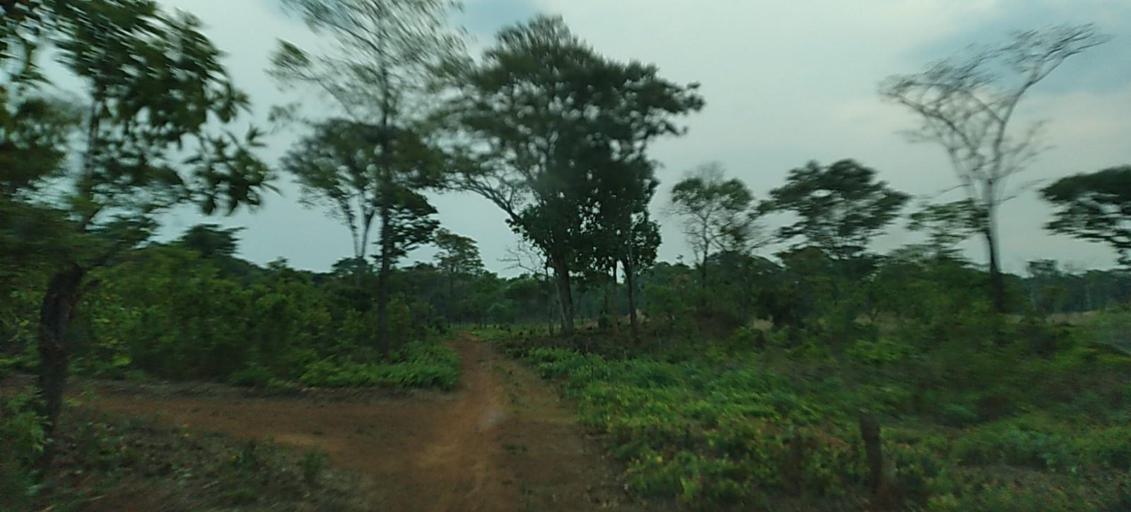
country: ZM
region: North-Western
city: Solwezi
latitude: -12.0439
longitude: 26.0039
